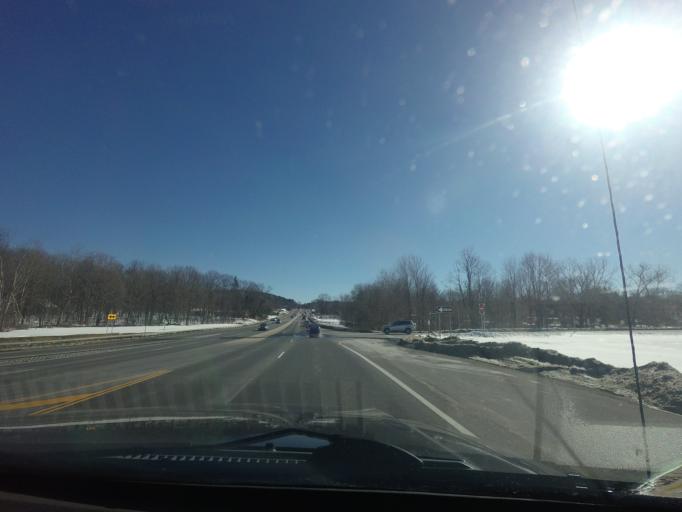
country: US
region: New York
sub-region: Rensselaer County
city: East Greenbush
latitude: 42.5565
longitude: -73.6783
